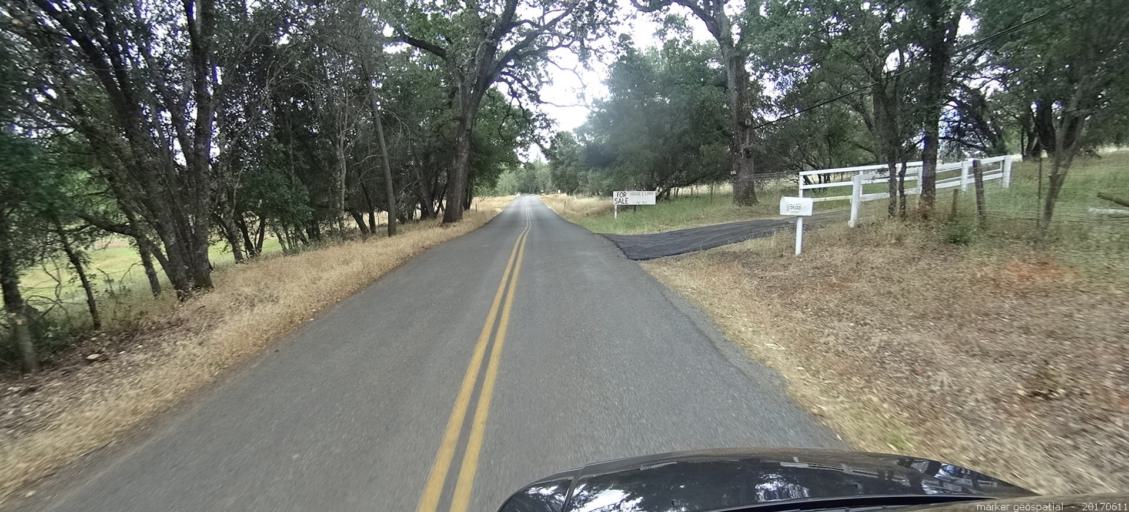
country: US
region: California
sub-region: Butte County
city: Oroville
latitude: 39.6327
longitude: -121.5285
